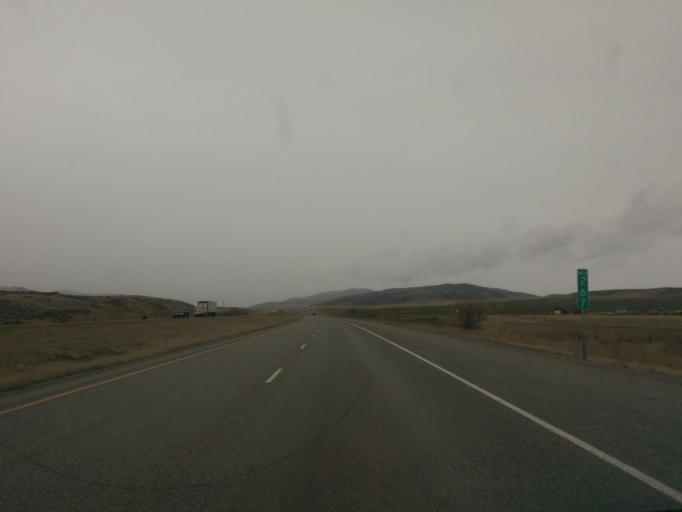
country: US
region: Montana
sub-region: Gallatin County
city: Three Forks
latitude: 45.9145
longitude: -111.7569
